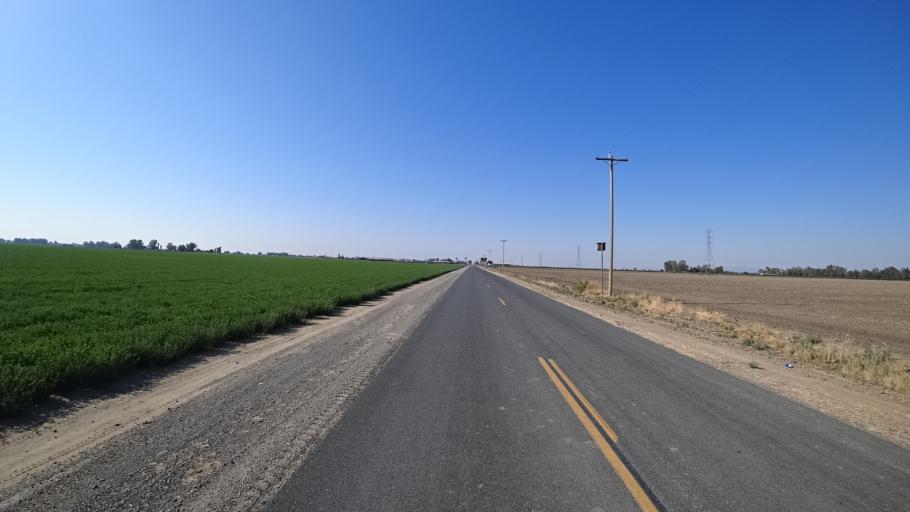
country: US
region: California
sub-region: Fresno County
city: Riverdale
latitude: 36.3578
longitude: -119.8872
